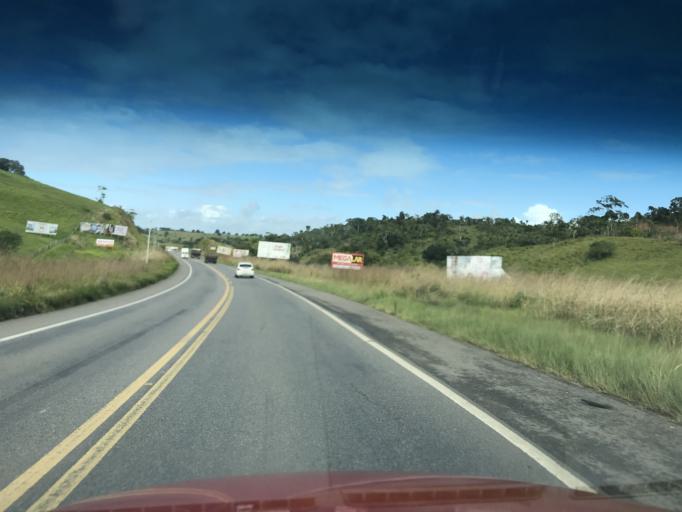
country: BR
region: Bahia
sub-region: Conceicao Do Almeida
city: Muritiba
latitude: -12.9252
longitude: -39.2509
